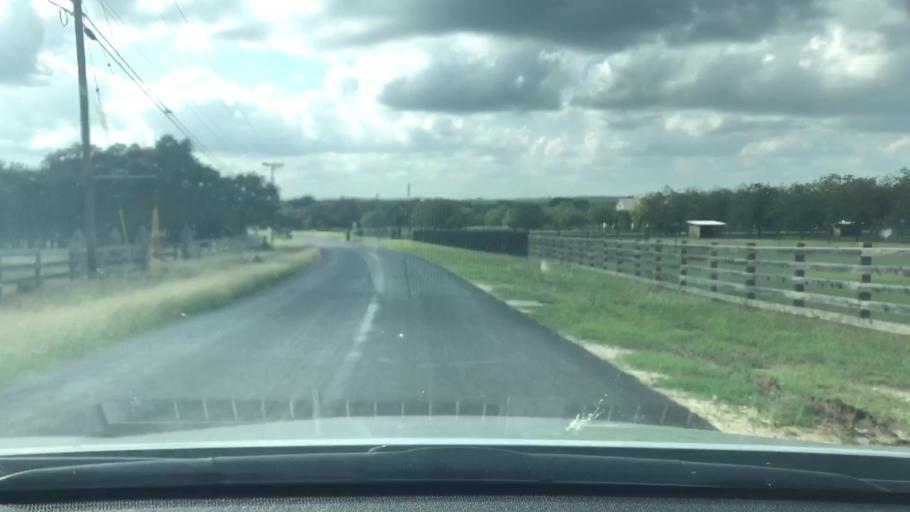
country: US
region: Texas
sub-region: Bexar County
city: Fair Oaks Ranch
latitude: 29.7677
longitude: -98.6304
